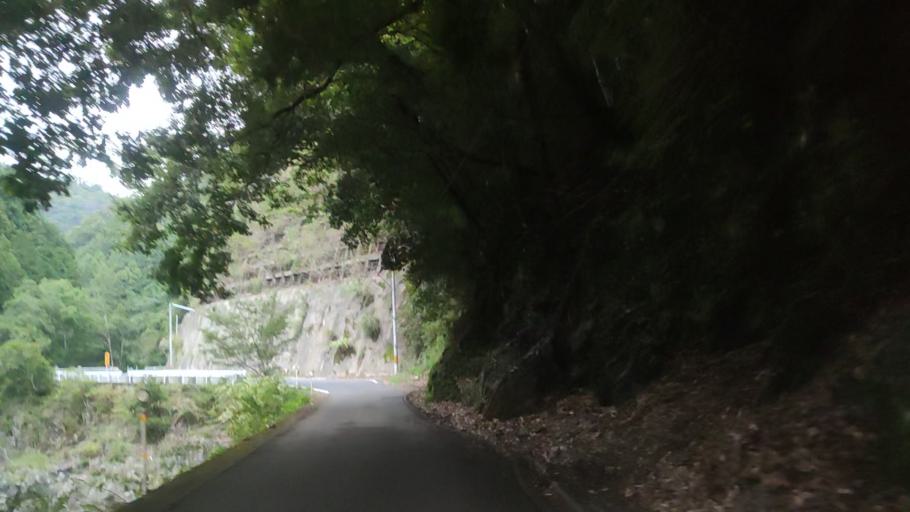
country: JP
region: Wakayama
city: Hashimoto
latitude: 34.2702
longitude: 135.6402
